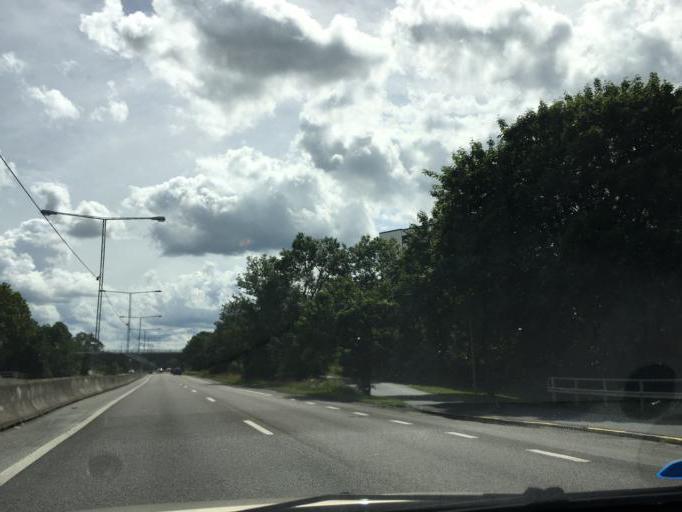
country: SE
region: Stockholm
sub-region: Stockholms Kommun
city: Bromma
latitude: 59.3550
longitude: 17.8790
